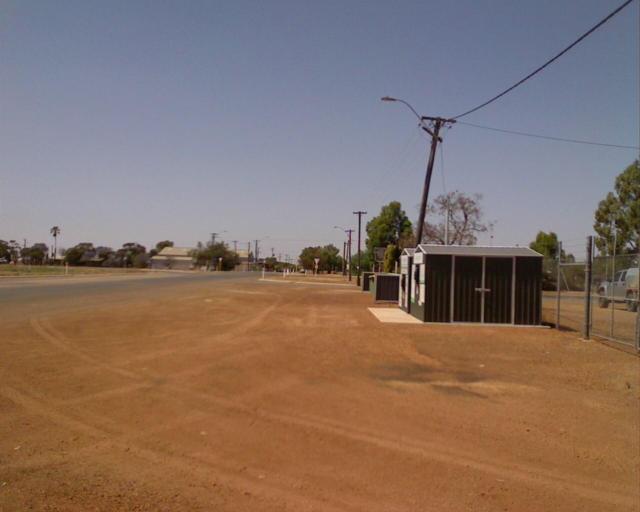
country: AU
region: Western Australia
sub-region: Merredin
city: Merredin
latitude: -30.9122
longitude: 118.2094
